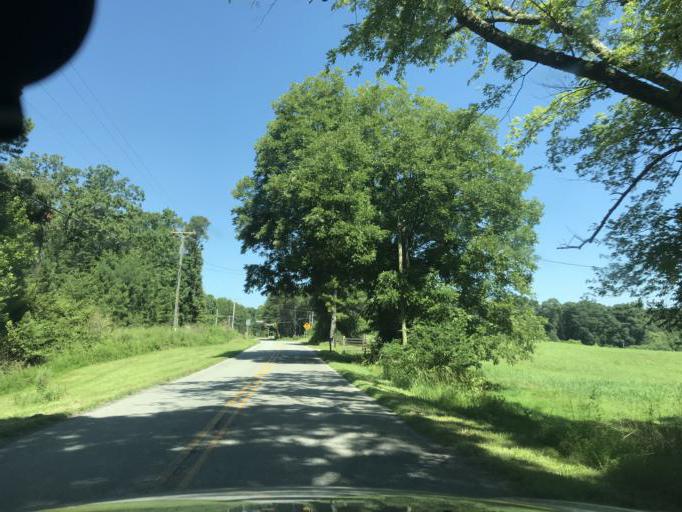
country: US
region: Georgia
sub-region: Forsyth County
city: Cumming
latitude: 34.2056
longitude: -84.1161
